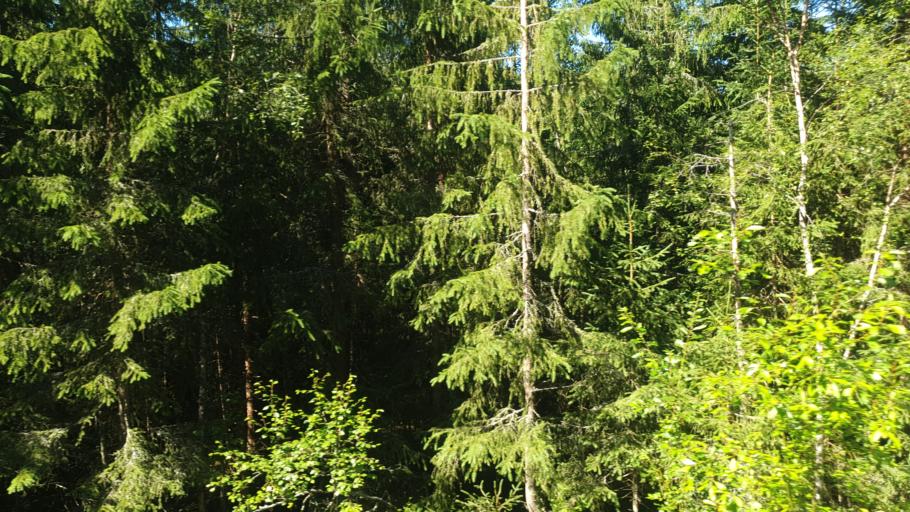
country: NO
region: Sor-Trondelag
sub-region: Meldal
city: Meldal
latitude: 63.1470
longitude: 9.7165
